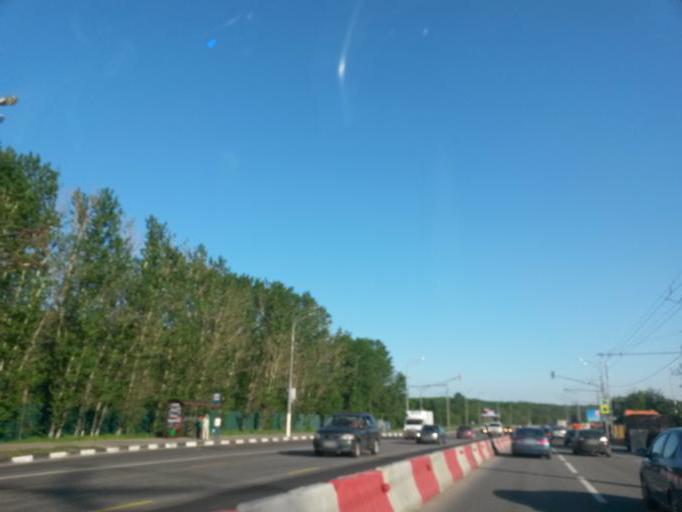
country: RU
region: Moscow
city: Orekhovo-Borisovo Severnoye
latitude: 55.6058
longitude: 37.6681
